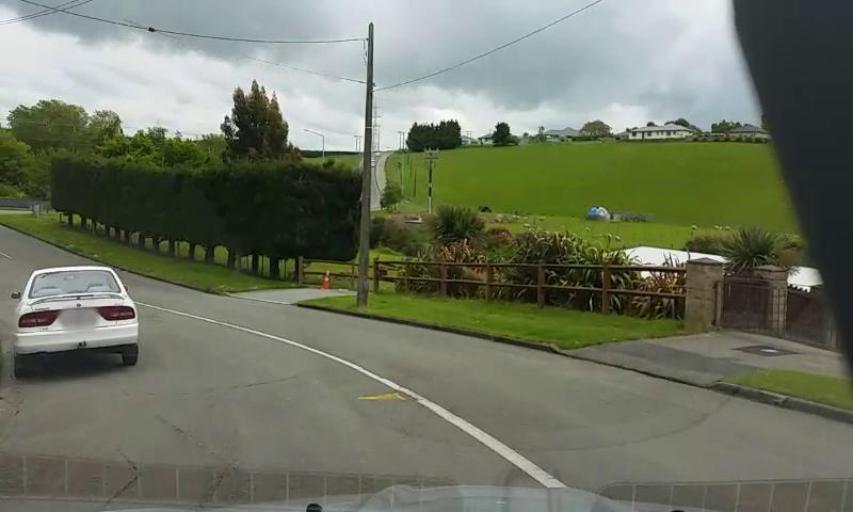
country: NZ
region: Canterbury
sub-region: Timaru District
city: Timaru
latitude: -44.3735
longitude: 171.2345
